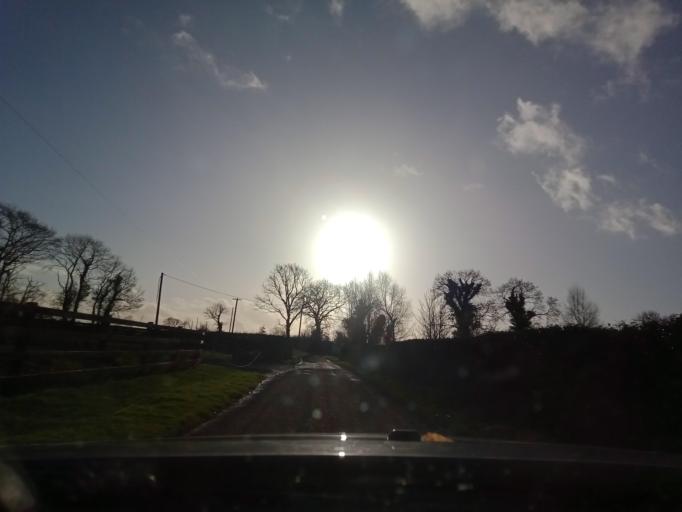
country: IE
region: Leinster
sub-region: Kilkenny
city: Callan
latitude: 52.4948
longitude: -7.3936
